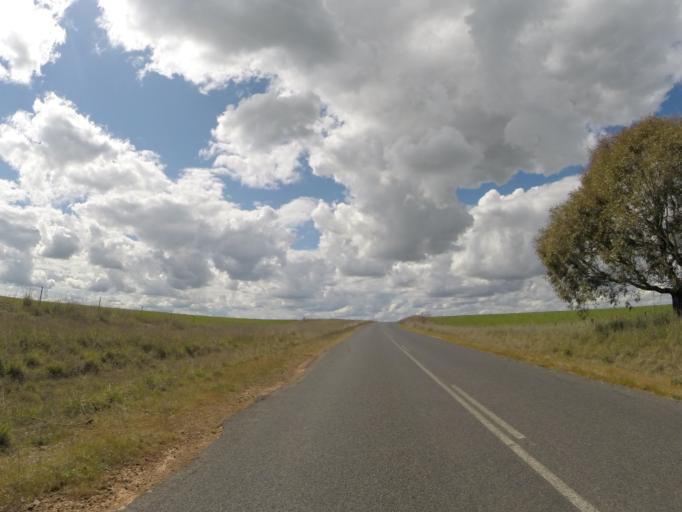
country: AU
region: New South Wales
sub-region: Yass Valley
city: Yass
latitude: -34.9084
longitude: 148.8863
